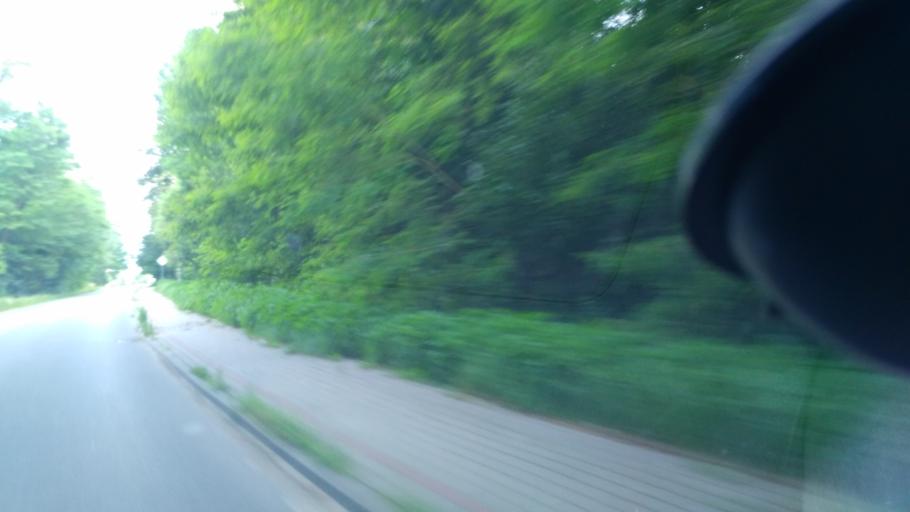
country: PL
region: Subcarpathian Voivodeship
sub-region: Powiat rzeszowski
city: Wysoka Glogowska
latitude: 50.1312
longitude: 22.0236
